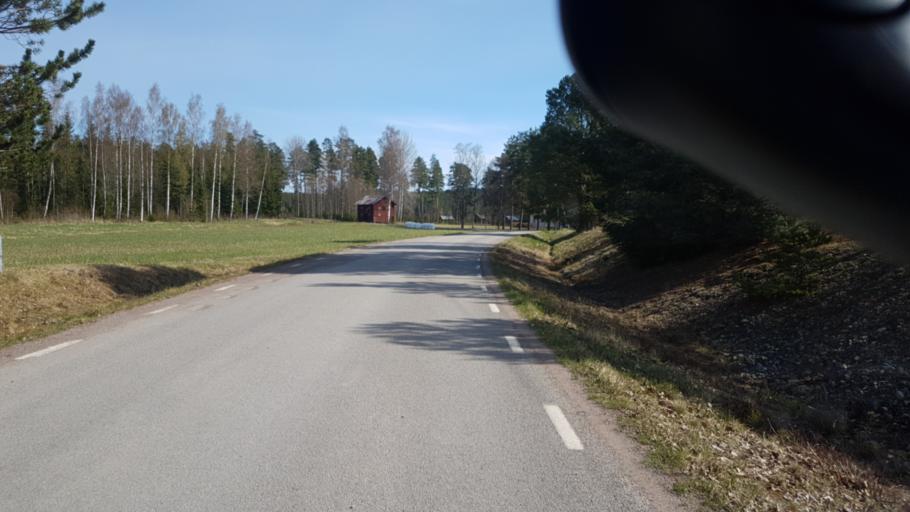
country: SE
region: Vaermland
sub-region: Arvika Kommun
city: Arvika
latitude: 59.5546
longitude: 12.7431
